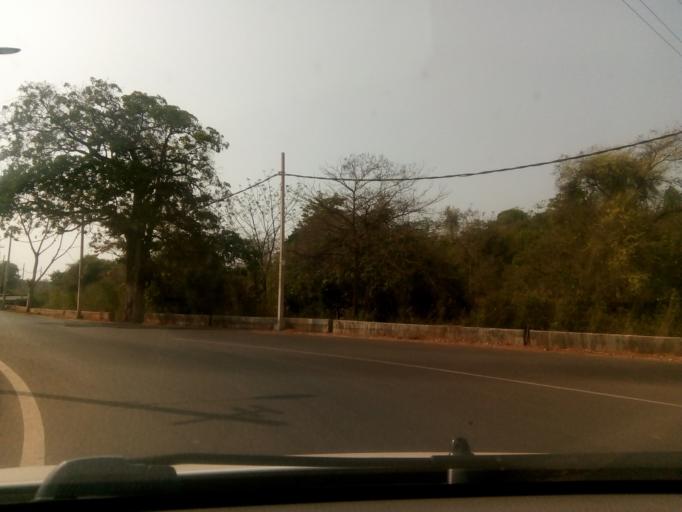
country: IN
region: Goa
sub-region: North Goa
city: Pernem
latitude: 15.7181
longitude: 73.8553
